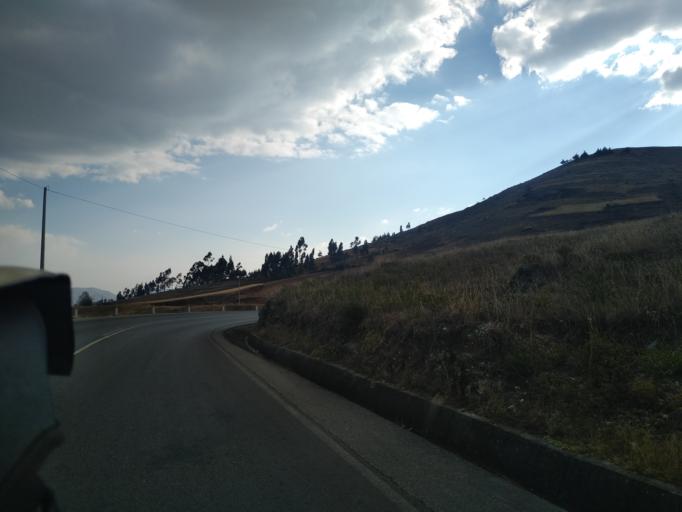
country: PE
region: Cajamarca
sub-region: Provincia de Cajamarca
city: Llacanora
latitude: -7.1488
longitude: -78.4112
